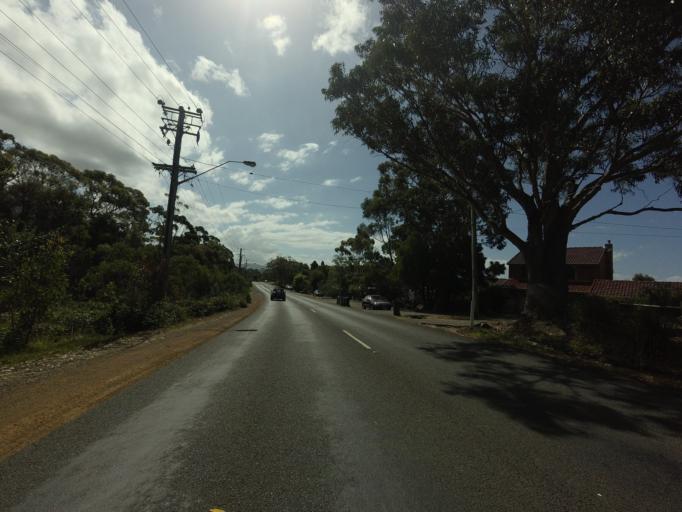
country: AU
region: Tasmania
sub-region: Hobart
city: Dynnyrne
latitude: -42.9162
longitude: 147.3174
